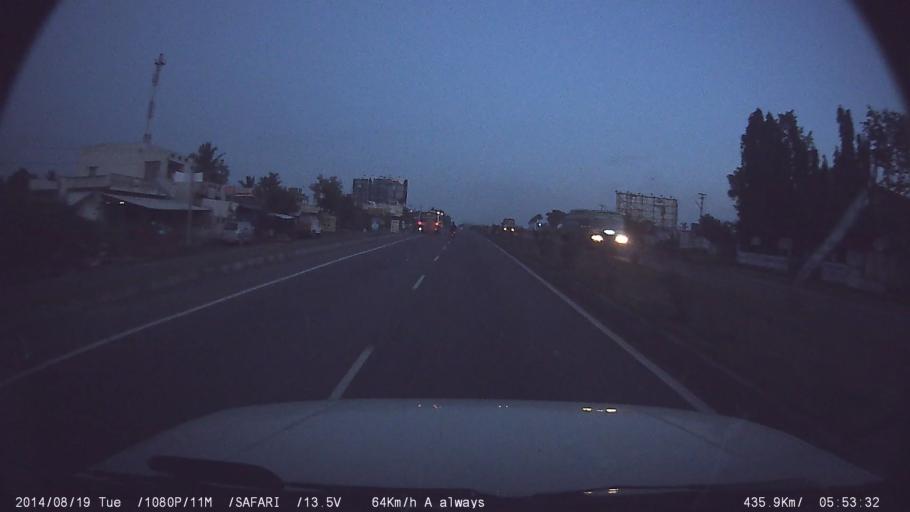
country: IN
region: Tamil Nadu
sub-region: Salem
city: Omalur
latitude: 11.7246
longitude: 78.0677
